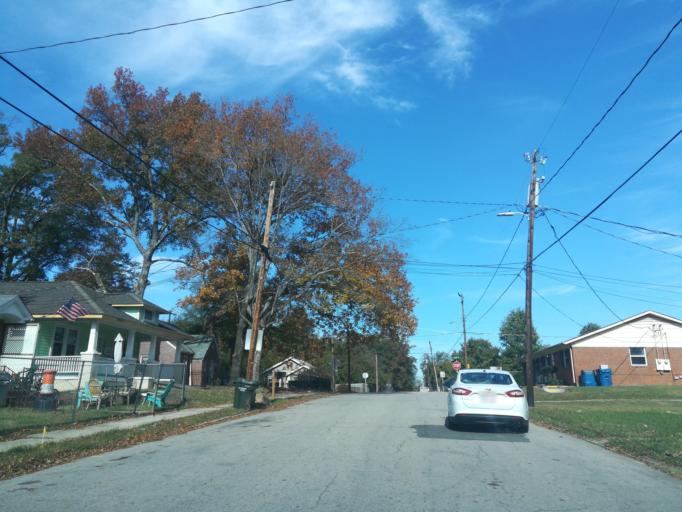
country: US
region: North Carolina
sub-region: Durham County
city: Durham
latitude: 35.9883
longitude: -78.8805
